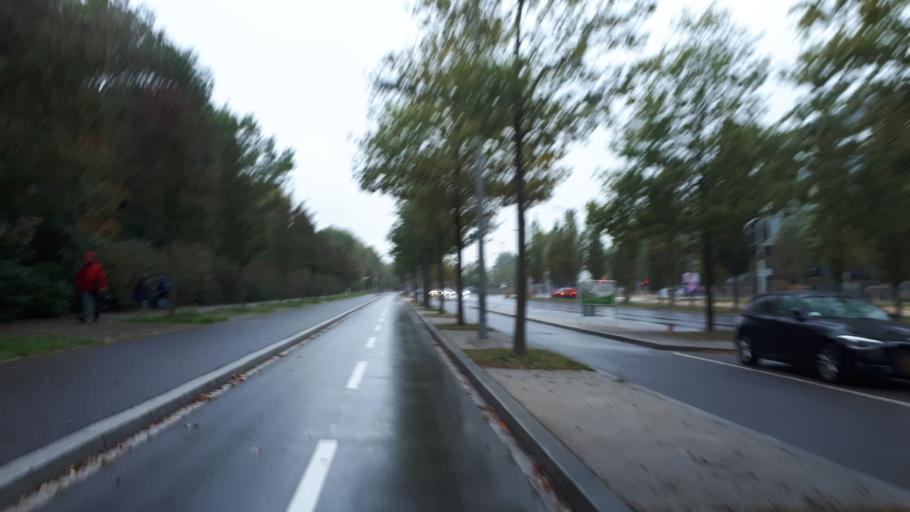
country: LU
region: Luxembourg
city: Kirchberg
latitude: 49.6270
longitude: 6.1632
